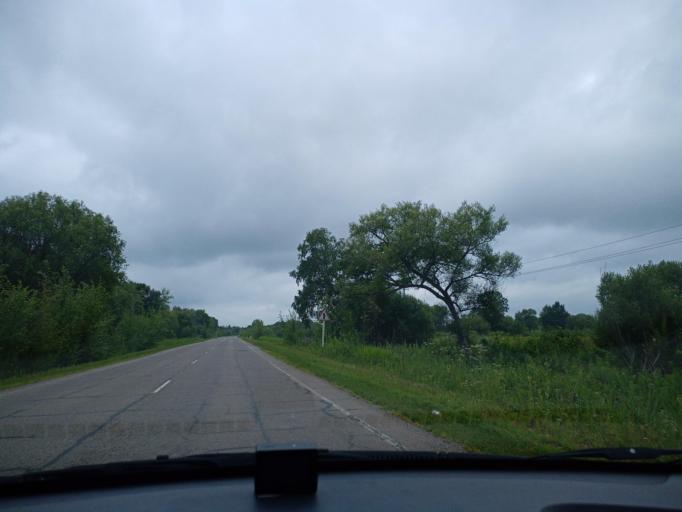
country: RU
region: Primorskiy
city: Novopokrovka
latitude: 45.8877
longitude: 134.8426
